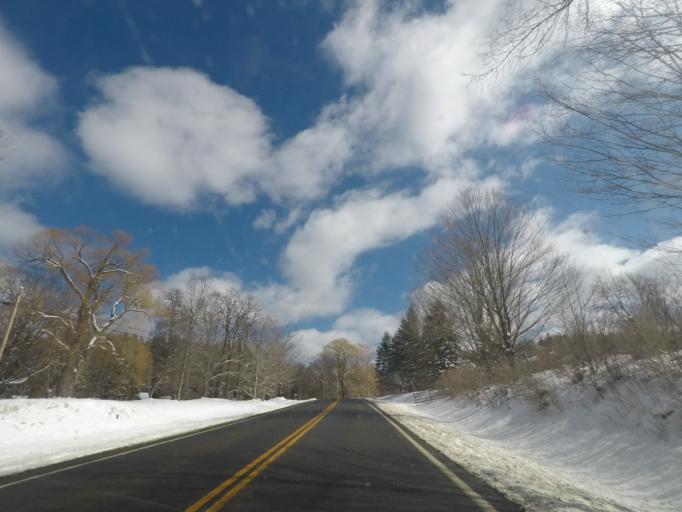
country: US
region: New York
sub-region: Rensselaer County
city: Nassau
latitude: 42.4599
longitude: -73.5466
